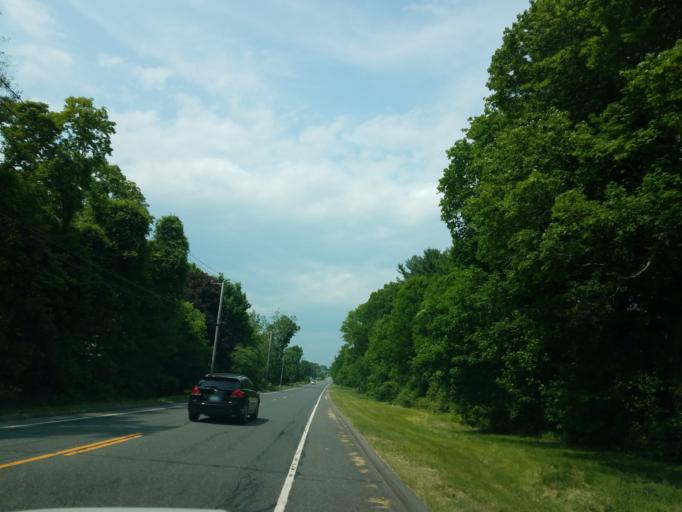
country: US
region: Connecticut
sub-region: Hartford County
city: Thompsonville
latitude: 42.0264
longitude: -72.6171
